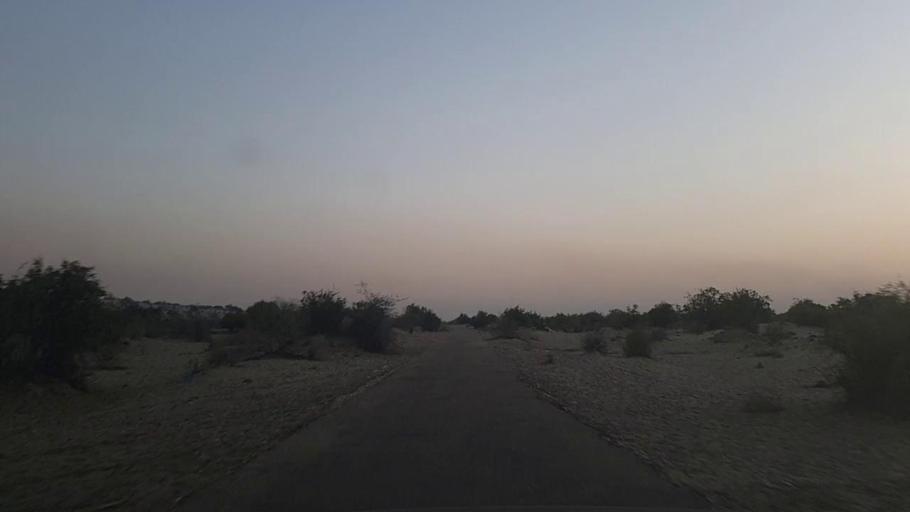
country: PK
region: Sindh
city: Jam Sahib
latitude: 26.3984
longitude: 68.8096
